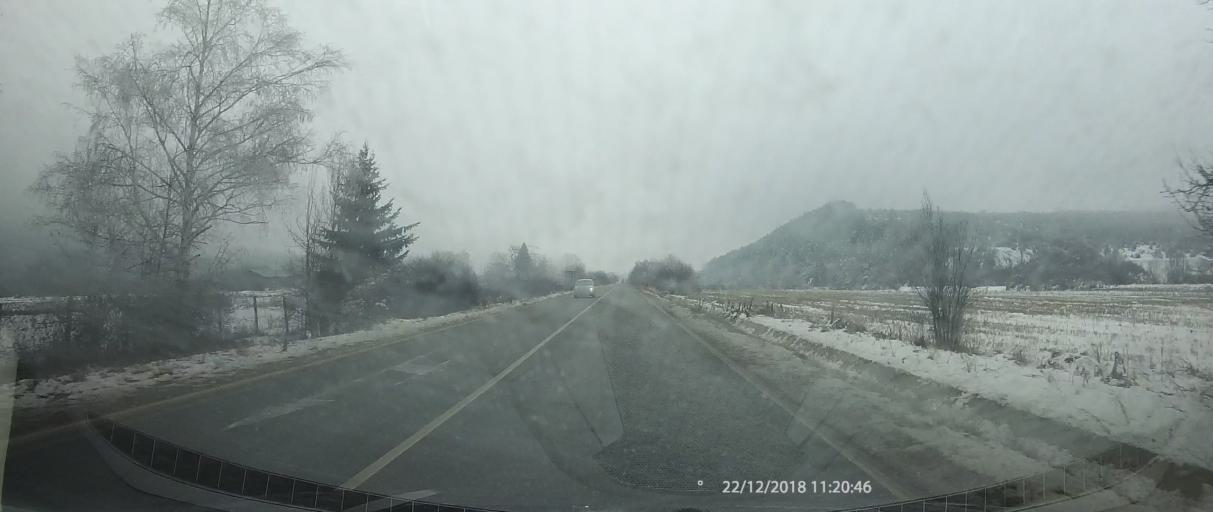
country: BG
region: Kyustendil
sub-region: Obshtina Kyustendil
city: Kyustendil
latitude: 42.2624
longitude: 22.8256
